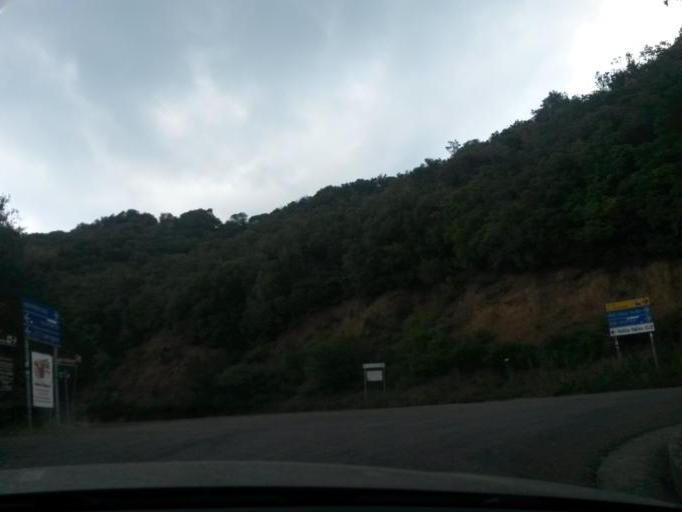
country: IT
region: Tuscany
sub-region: Provincia di Livorno
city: Rio nell'Elba
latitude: 42.8240
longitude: 10.3934
